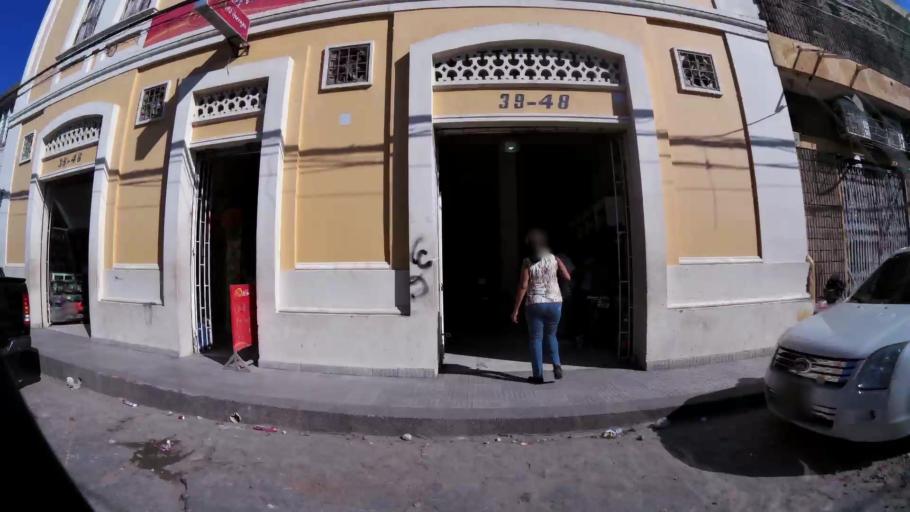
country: CO
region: Atlantico
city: Barranquilla
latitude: 10.9780
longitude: -74.7777
